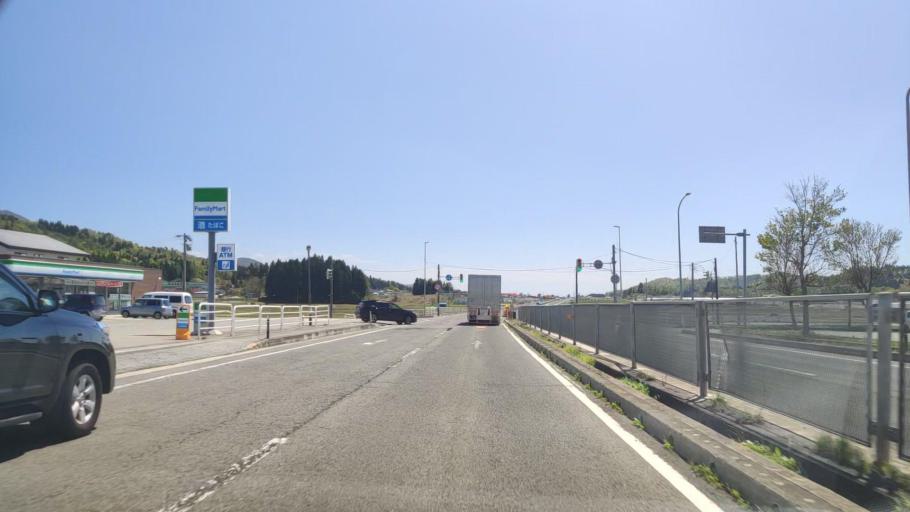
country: JP
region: Yamagata
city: Obanazawa
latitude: 38.5463
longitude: 140.3963
